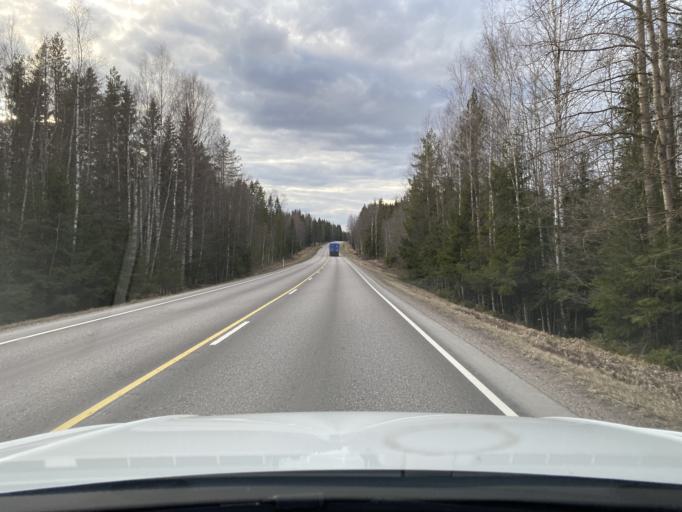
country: FI
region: Haeme
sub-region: Haemeenlinna
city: Renko
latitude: 60.8025
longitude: 24.0779
